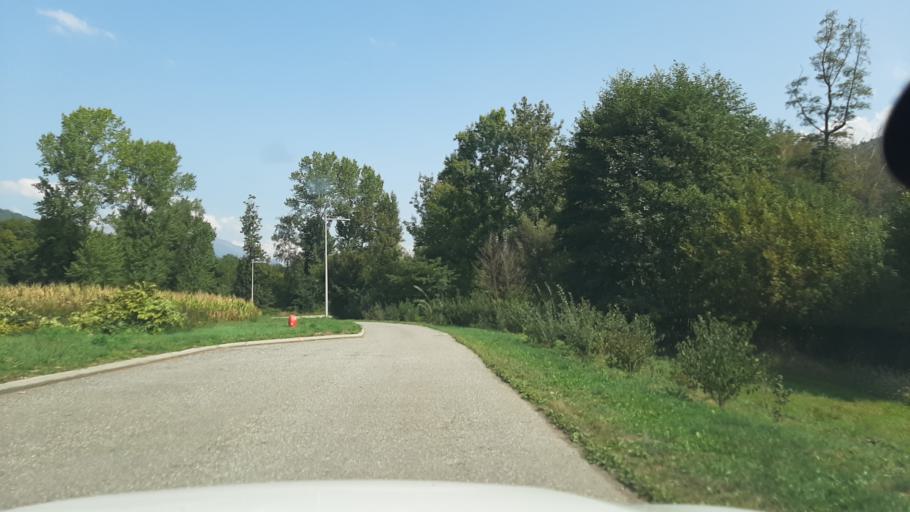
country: FR
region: Rhone-Alpes
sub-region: Departement de la Savoie
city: La Rochette
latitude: 45.4706
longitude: 6.1279
